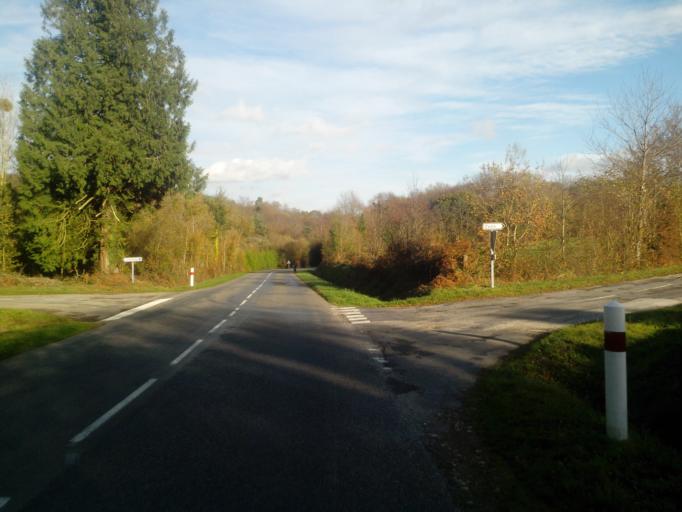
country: FR
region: Brittany
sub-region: Departement du Morbihan
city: Guilliers
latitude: 48.0237
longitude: -2.4573
